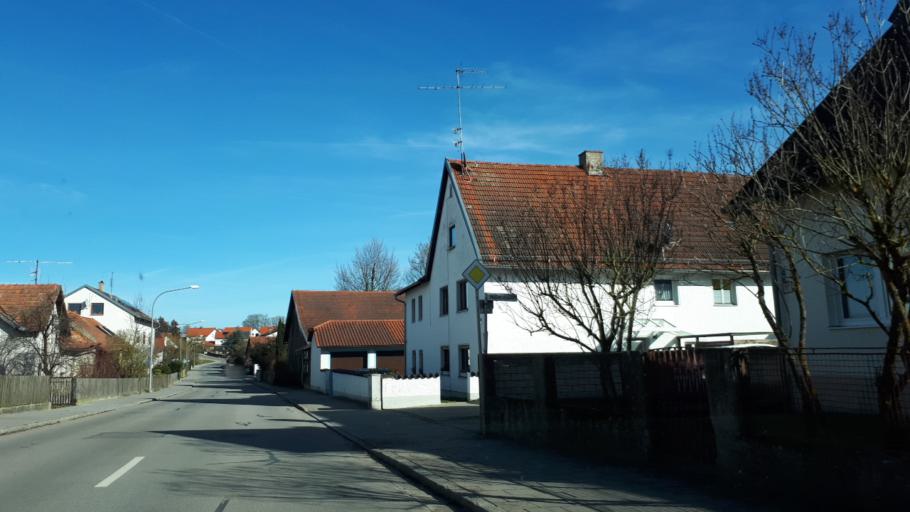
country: DE
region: Bavaria
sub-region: Upper Palatinate
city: Pentling
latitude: 48.9709
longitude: 12.0550
